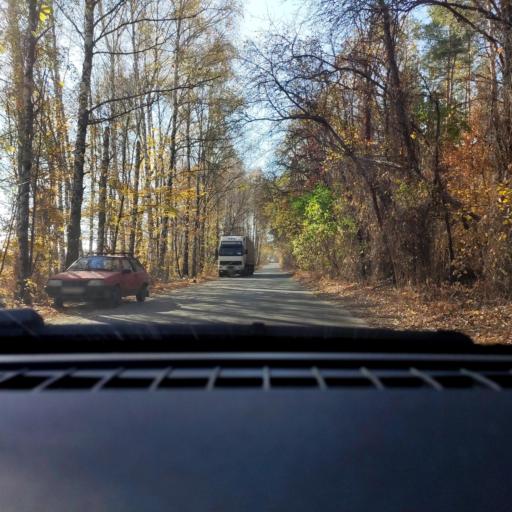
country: RU
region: Voronezj
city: Somovo
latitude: 51.6858
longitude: 39.2999
